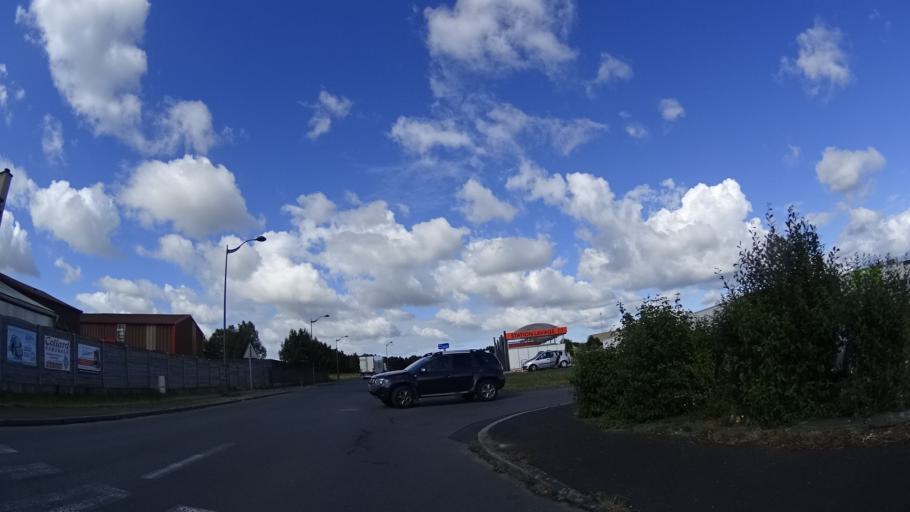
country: FR
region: Brittany
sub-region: Departement d'Ille-et-Vilaine
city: Hede-Bazouges
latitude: 48.3022
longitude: -1.8172
